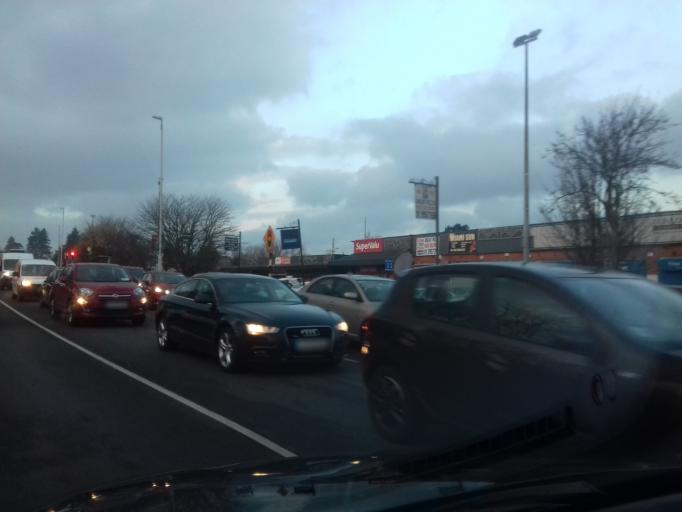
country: IE
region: Leinster
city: Sandyford
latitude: 53.2755
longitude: -6.2238
